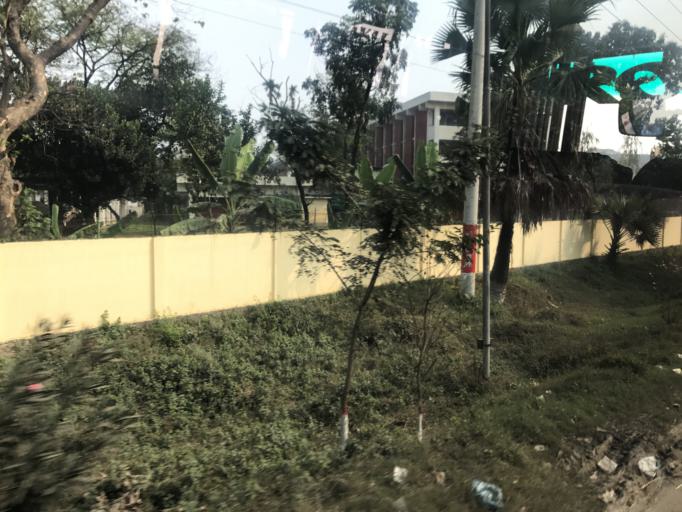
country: BD
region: Dhaka
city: Tungi
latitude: 23.9047
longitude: 90.2678
